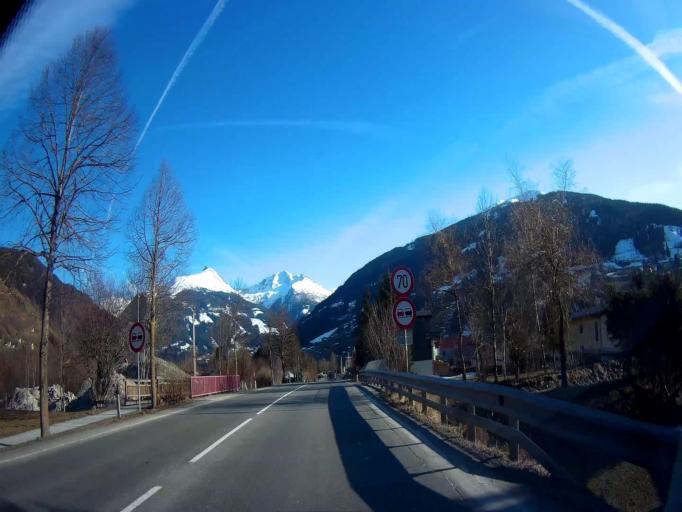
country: AT
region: Salzburg
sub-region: Politischer Bezirk Sankt Johann im Pongau
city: Bad Hofgastein
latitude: 47.1527
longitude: 13.1123
